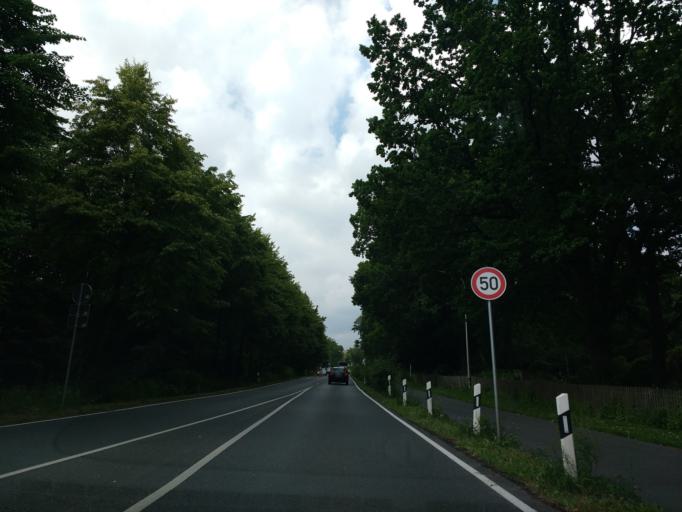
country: DE
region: North Rhine-Westphalia
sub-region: Regierungsbezirk Detmold
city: Lemgo
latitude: 52.0383
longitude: 8.9026
